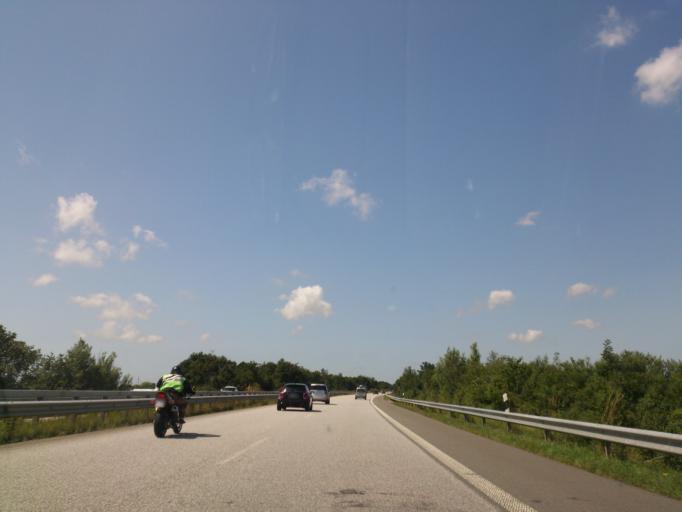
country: DE
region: Schleswig-Holstein
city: Heide
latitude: 54.1671
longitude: 9.1053
